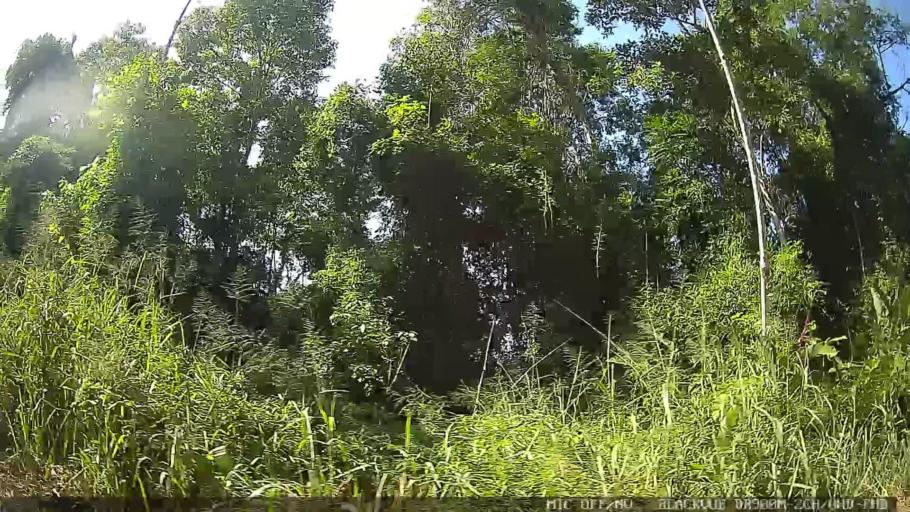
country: BR
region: Sao Paulo
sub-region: Santos
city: Santos
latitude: -23.9985
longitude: -46.3114
